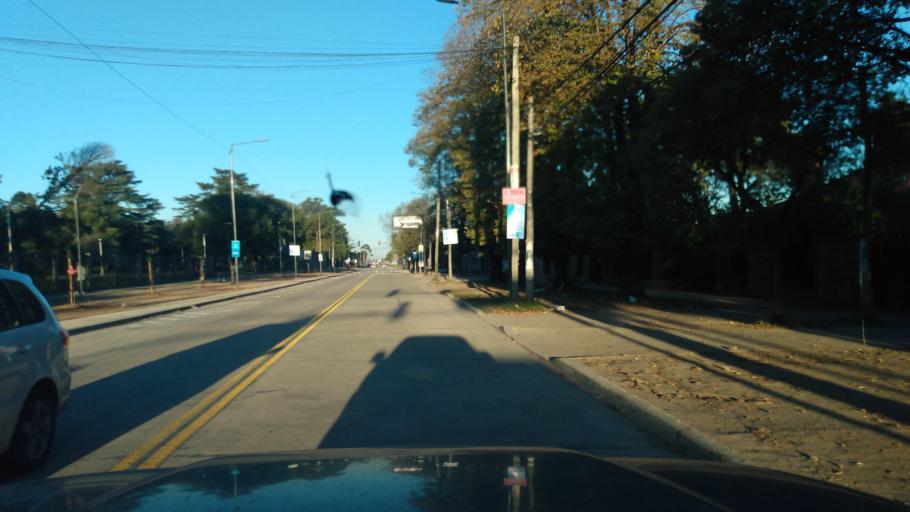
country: AR
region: Buenos Aires
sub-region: Partido de Merlo
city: Merlo
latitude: -34.6521
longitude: -58.7789
